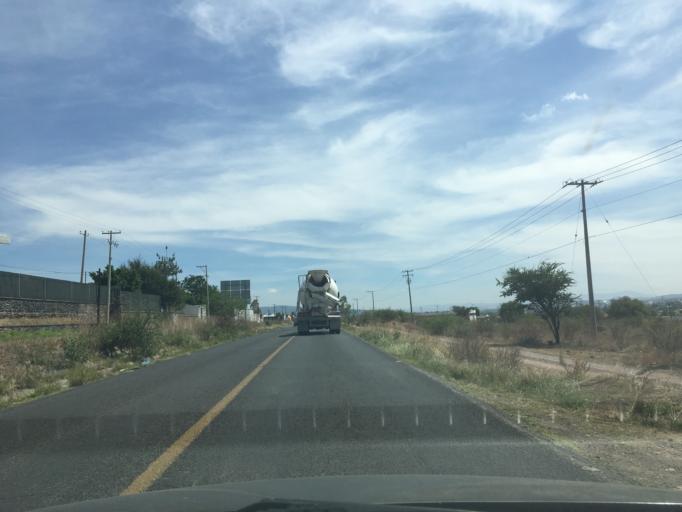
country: MX
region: Queretaro
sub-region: San Juan del Rio
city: Vista Hermosa (Cuasinada)
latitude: 20.3731
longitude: -100.0174
